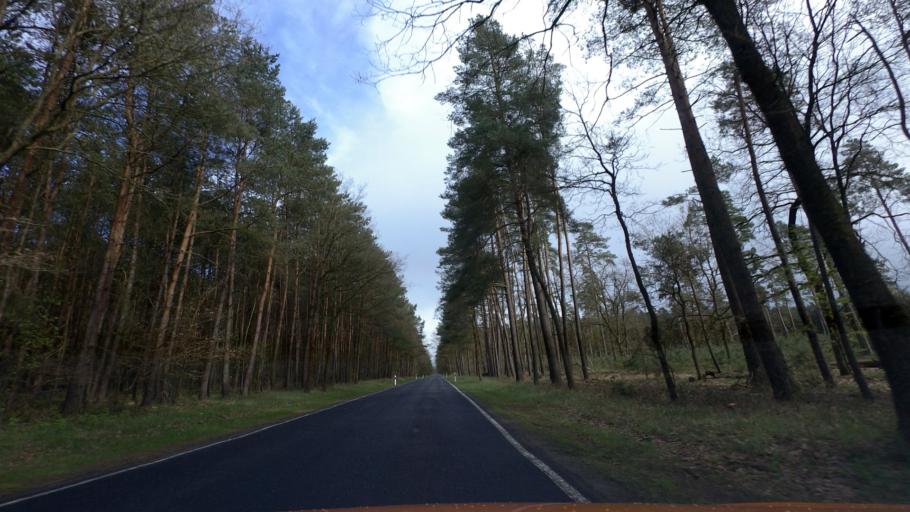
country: DE
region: Mecklenburg-Vorpommern
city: Nostorf
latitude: 53.4281
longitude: 10.6989
